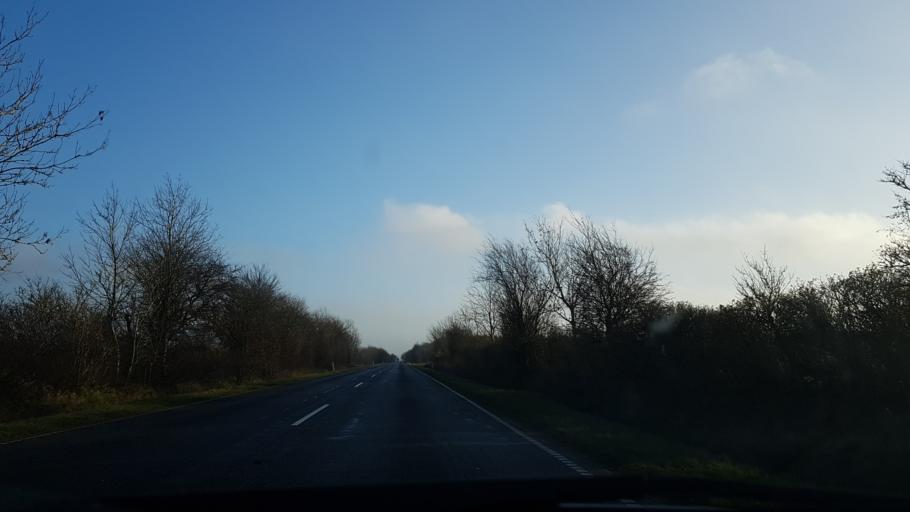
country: DK
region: South Denmark
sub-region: Haderslev Kommune
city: Vojens
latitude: 55.1840
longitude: 9.2278
